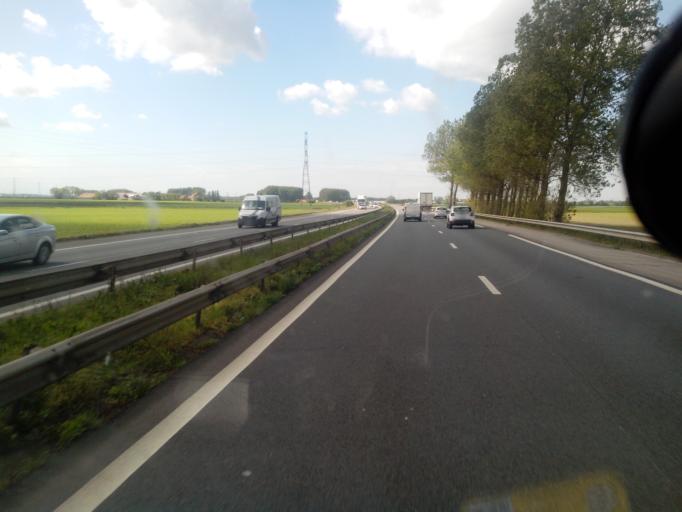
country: FR
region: Nord-Pas-de-Calais
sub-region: Departement du Nord
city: Bierne
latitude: 50.9790
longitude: 2.3857
